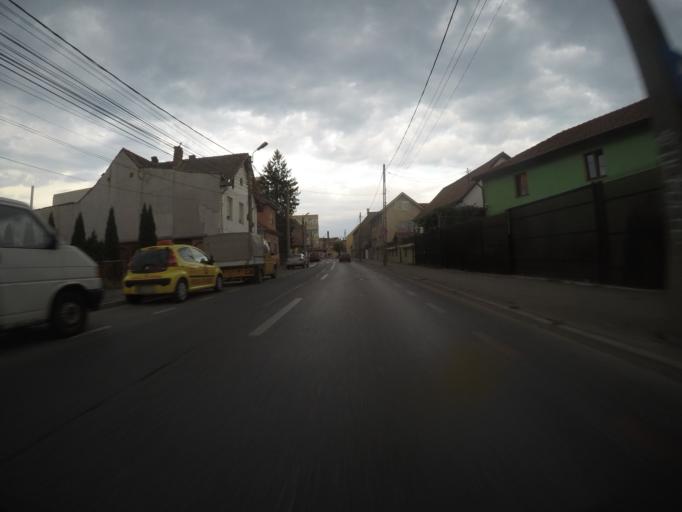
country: RO
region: Sibiu
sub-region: Municipiul Sibiu
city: Sibiu
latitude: 45.8024
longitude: 24.1531
